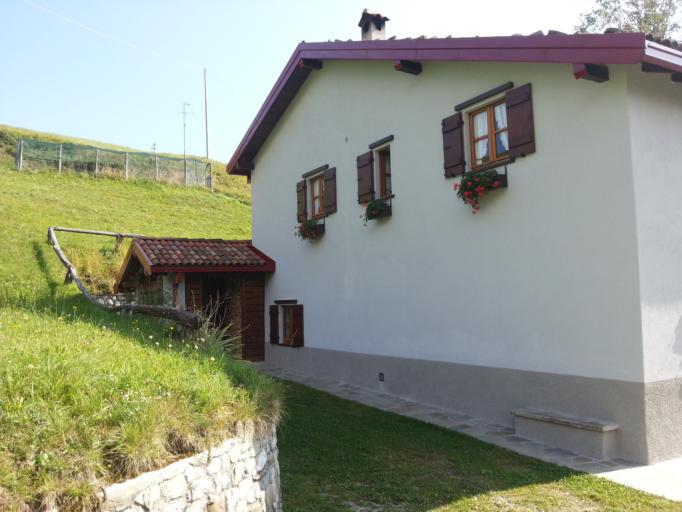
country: IT
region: Lombardy
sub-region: Provincia di Lecco
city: Pasturo
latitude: 45.9425
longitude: 9.4325
